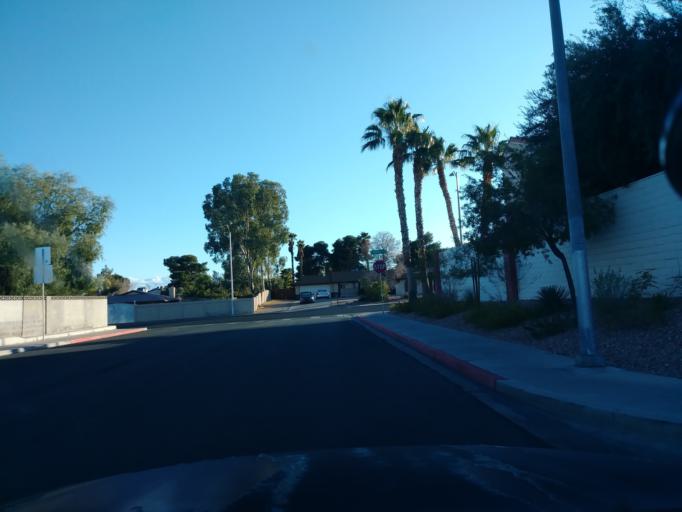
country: US
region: Nevada
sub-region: Clark County
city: Spring Valley
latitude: 36.1521
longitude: -115.2412
